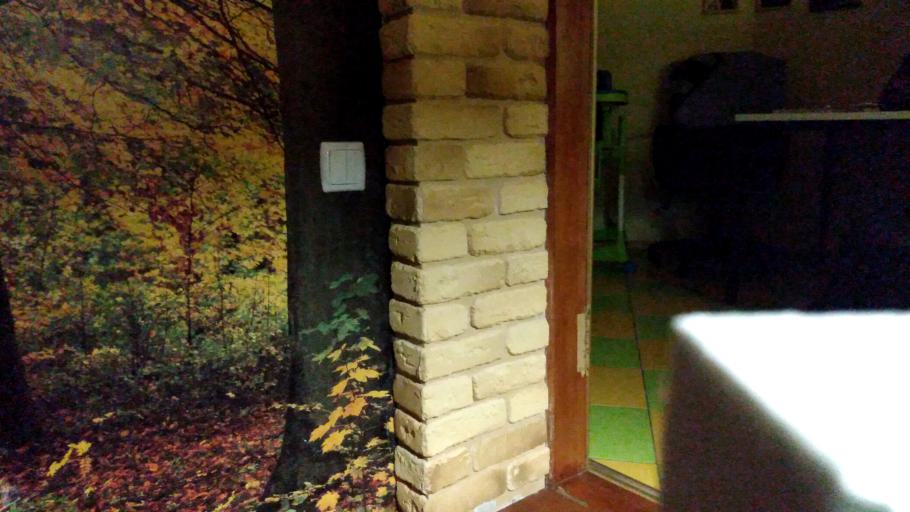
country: RU
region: Vologda
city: Lipin Bor
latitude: 60.7757
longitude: 38.0419
